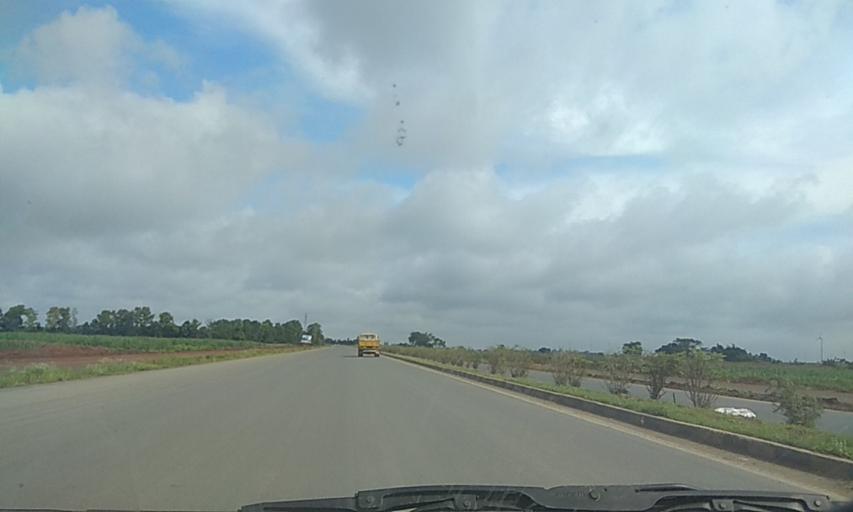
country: IN
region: Karnataka
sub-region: Haveri
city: Shiggaon
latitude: 15.0492
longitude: 75.1690
